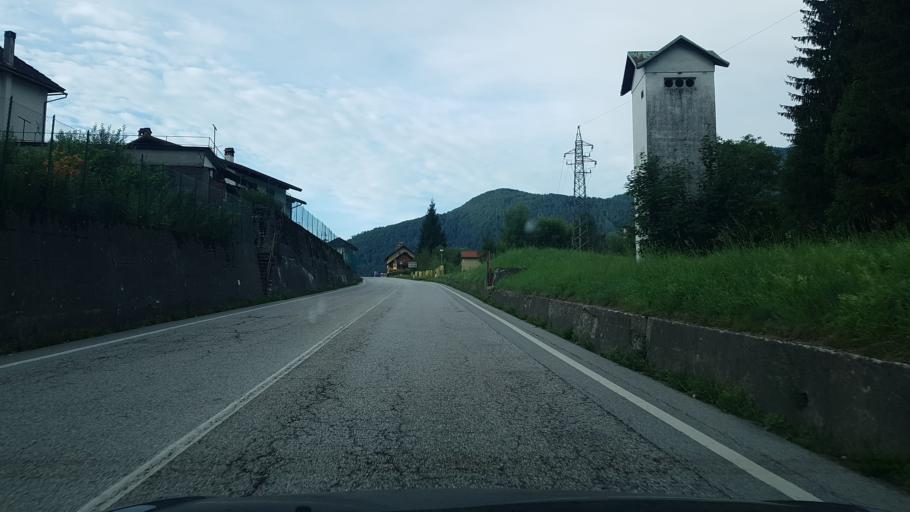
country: IT
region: Friuli Venezia Giulia
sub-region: Provincia di Udine
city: Ovaro
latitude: 46.4911
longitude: 12.8656
